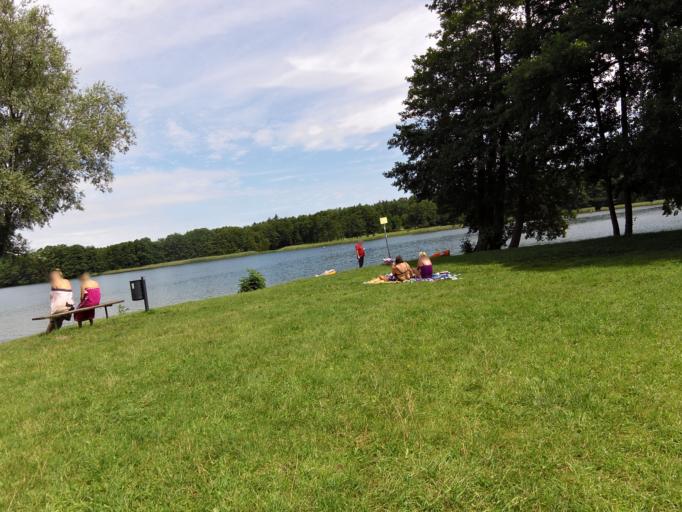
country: DE
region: Mecklenburg-Vorpommern
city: Loitz
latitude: 53.3438
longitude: 13.4446
